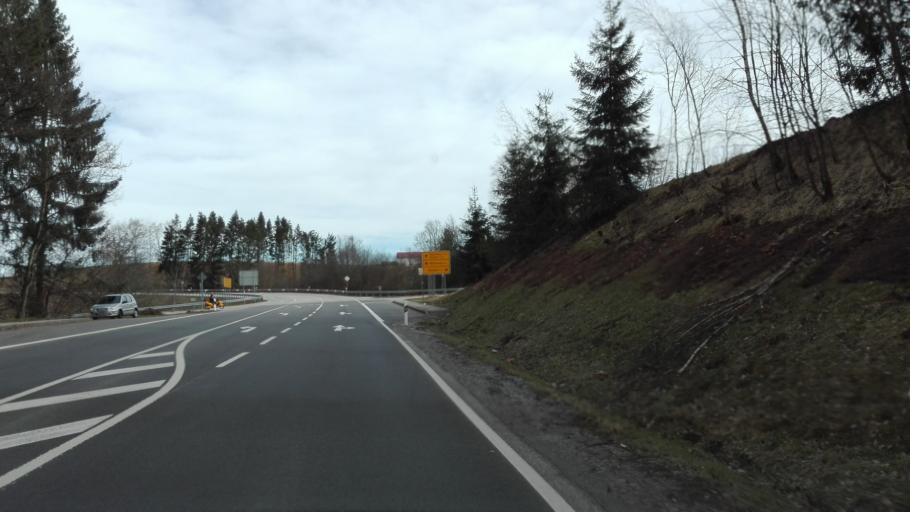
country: DE
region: Bavaria
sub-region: Lower Bavaria
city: Hauzenberg
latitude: 48.6312
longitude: 13.5861
